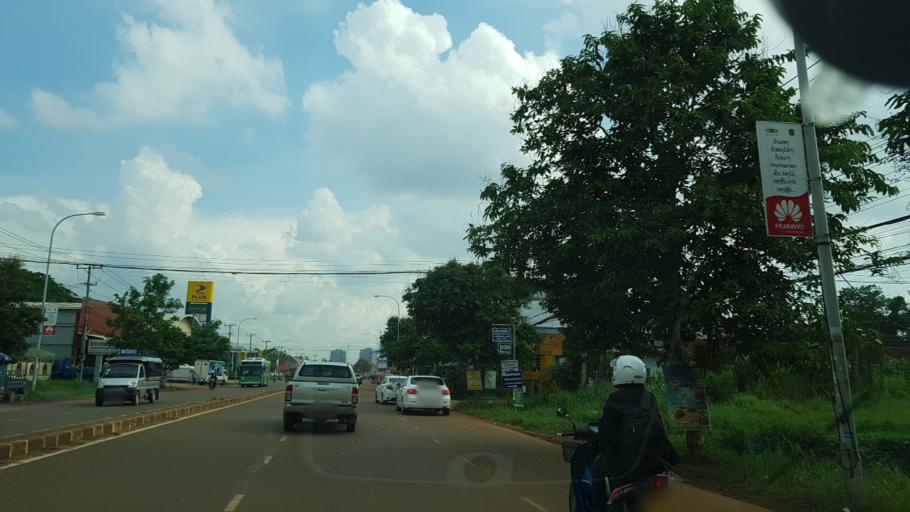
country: LA
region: Vientiane
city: Vientiane
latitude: 18.0189
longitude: 102.6508
